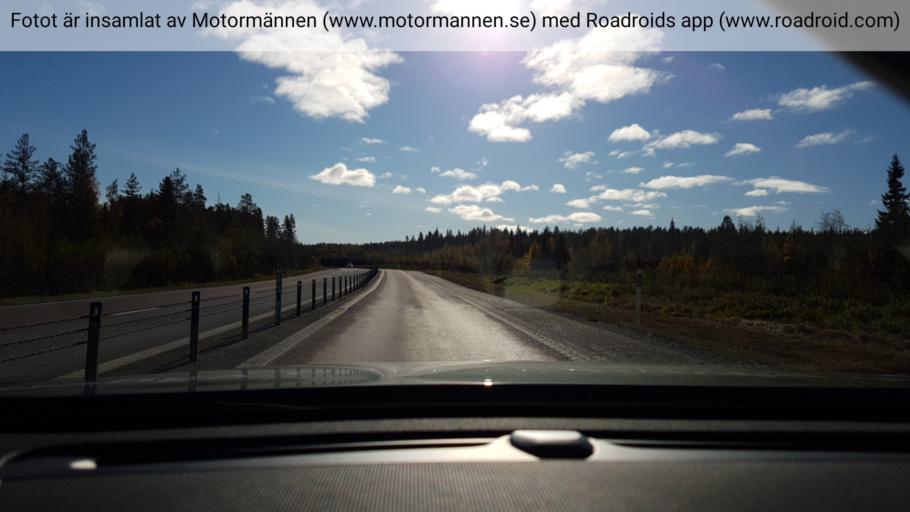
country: SE
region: Vaesterbotten
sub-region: Skelleftea Kommun
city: Skelleftea
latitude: 64.7013
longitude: 21.0037
